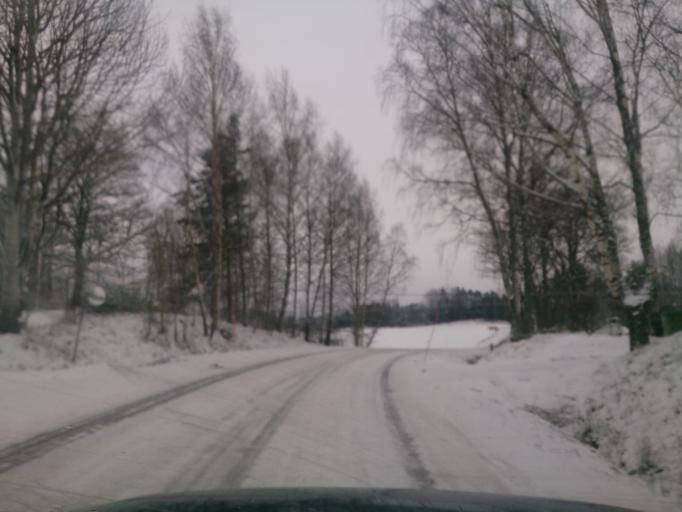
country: SE
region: OEstergoetland
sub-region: Norrkopings Kommun
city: Kimstad
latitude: 58.4221
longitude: 15.9130
